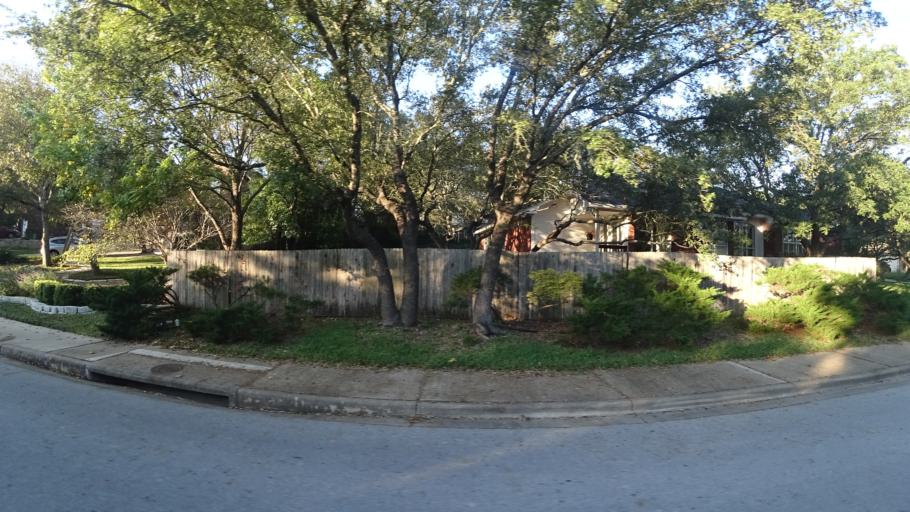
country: US
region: Texas
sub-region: Travis County
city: Hudson Bend
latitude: 30.3806
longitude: -97.8906
